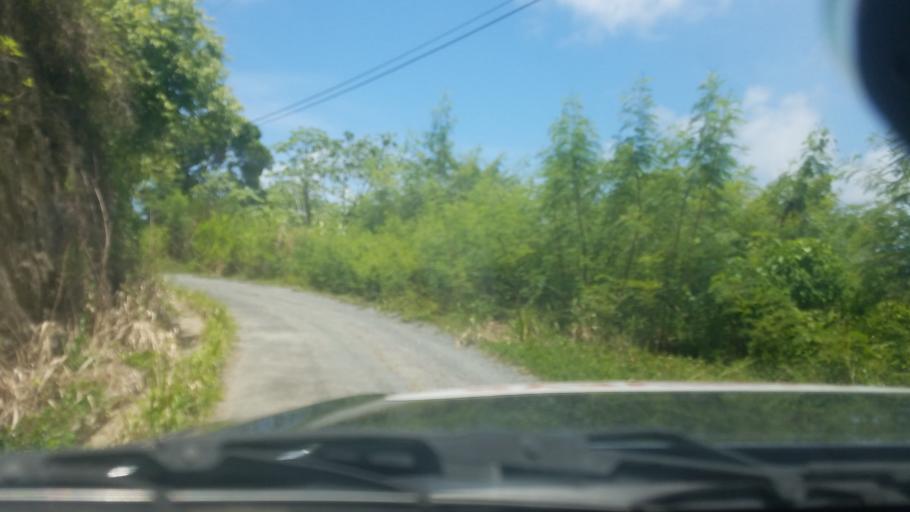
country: LC
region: Praslin
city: Praslin
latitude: 13.8689
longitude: -60.9148
